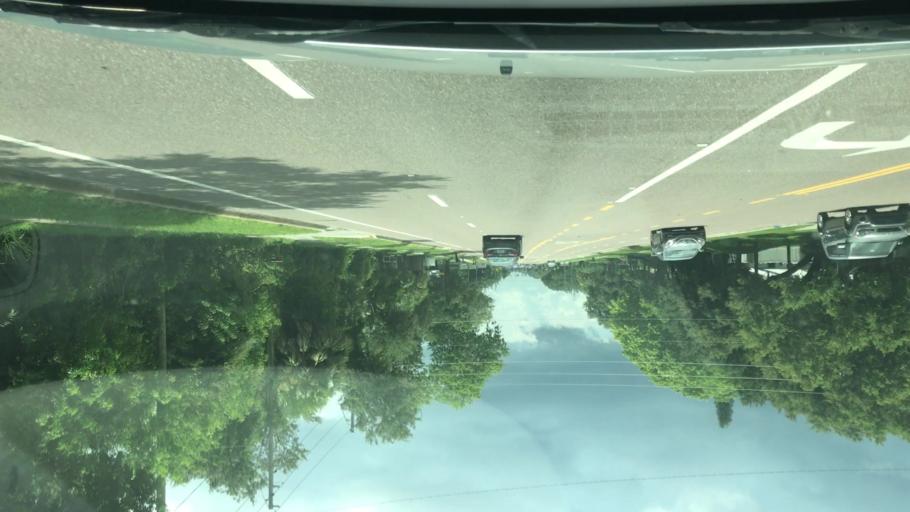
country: US
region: Florida
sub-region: Pinellas County
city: Kenneth City
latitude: 27.8209
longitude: -82.7415
